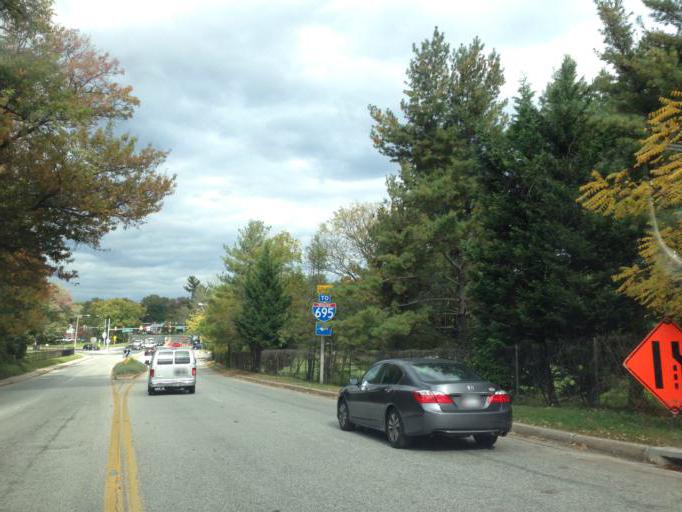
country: US
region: Maryland
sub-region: Baltimore County
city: Pikesville
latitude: 39.3786
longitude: -76.7182
